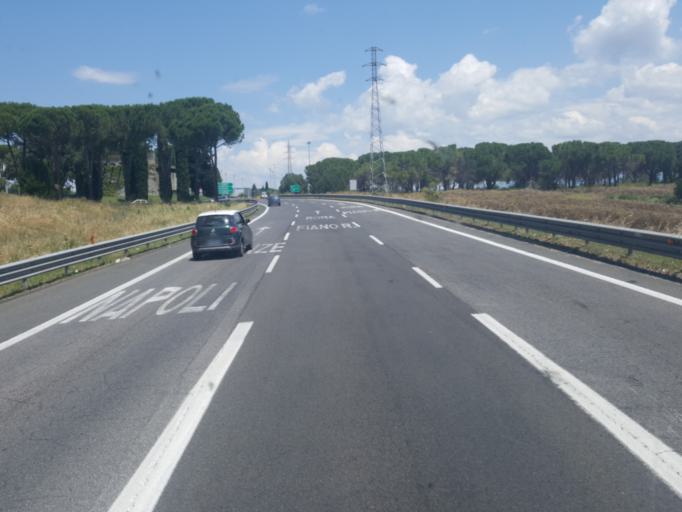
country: IT
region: Latium
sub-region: Citta metropolitana di Roma Capitale
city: Bivio di Capanelle
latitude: 42.1352
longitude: 12.6046
